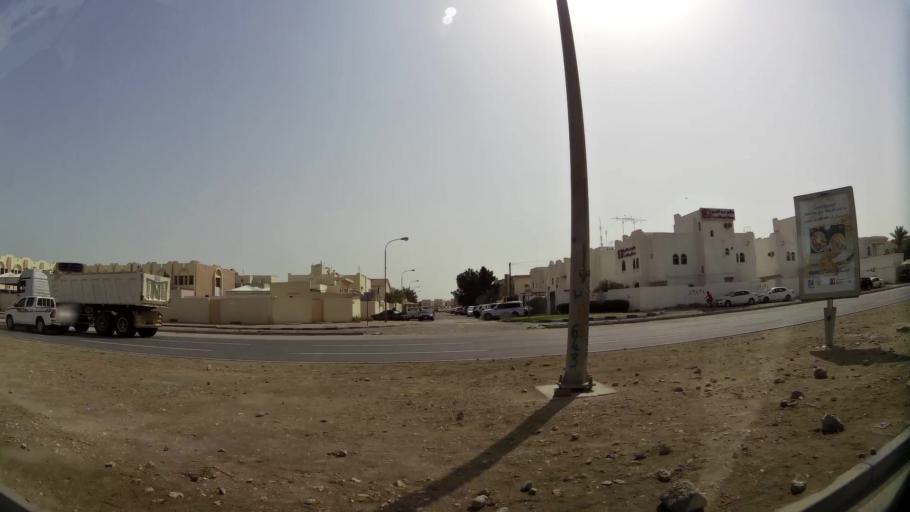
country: QA
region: Baladiyat ad Dawhah
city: Doha
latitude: 25.2434
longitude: 51.5242
